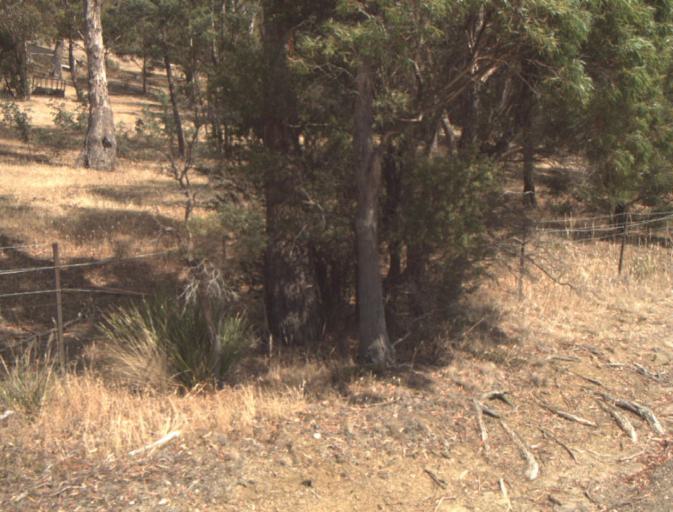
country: AU
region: Tasmania
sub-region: Launceston
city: Newstead
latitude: -41.4443
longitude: 147.2132
